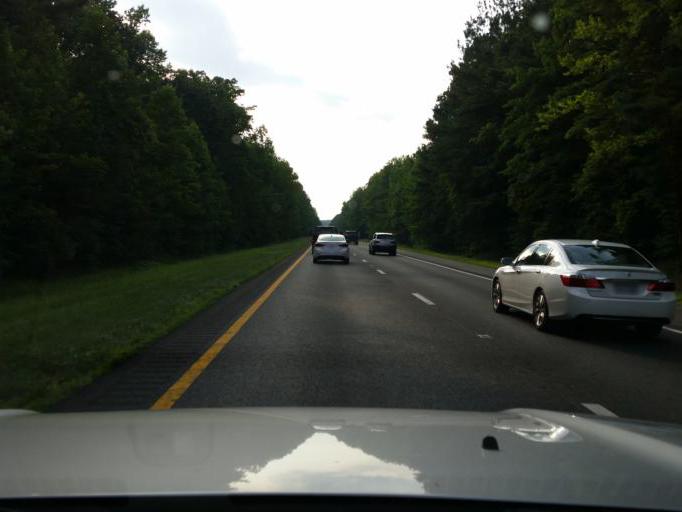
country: US
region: Virginia
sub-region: New Kent County
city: New Kent
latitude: 37.4666
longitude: -76.8934
